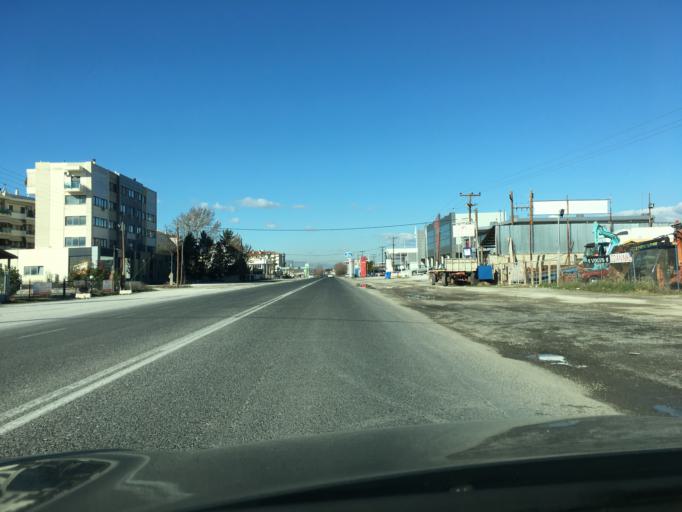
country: GR
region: Thessaly
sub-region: Nomos Larisis
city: Larisa
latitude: 39.6100
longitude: 22.4367
